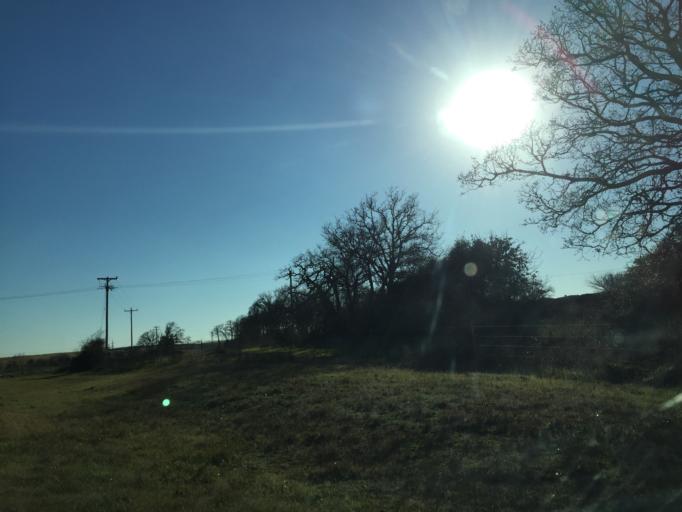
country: US
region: Texas
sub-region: Bastrop County
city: Elgin
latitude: 30.3826
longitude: -97.2443
